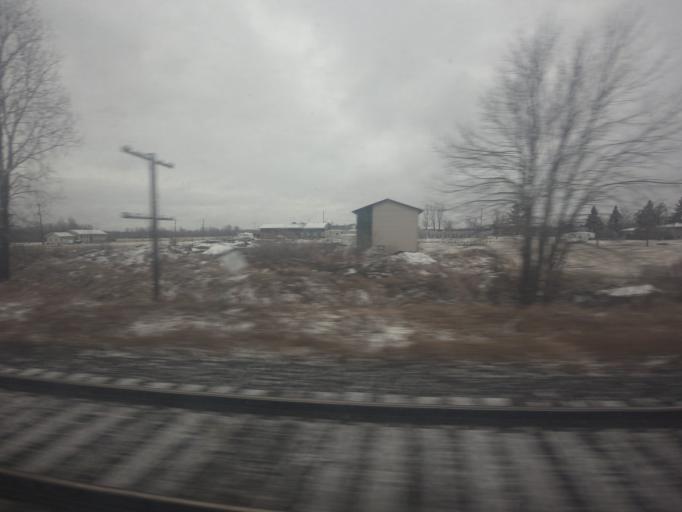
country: CA
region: Ontario
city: Gananoque
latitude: 44.3703
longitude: -76.1402
